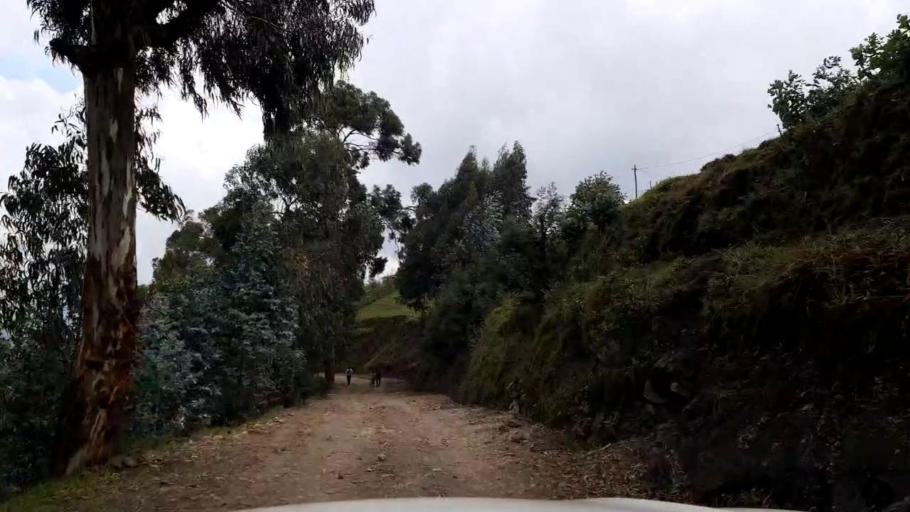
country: RW
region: Western Province
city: Kibuye
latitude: -1.9432
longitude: 29.4678
